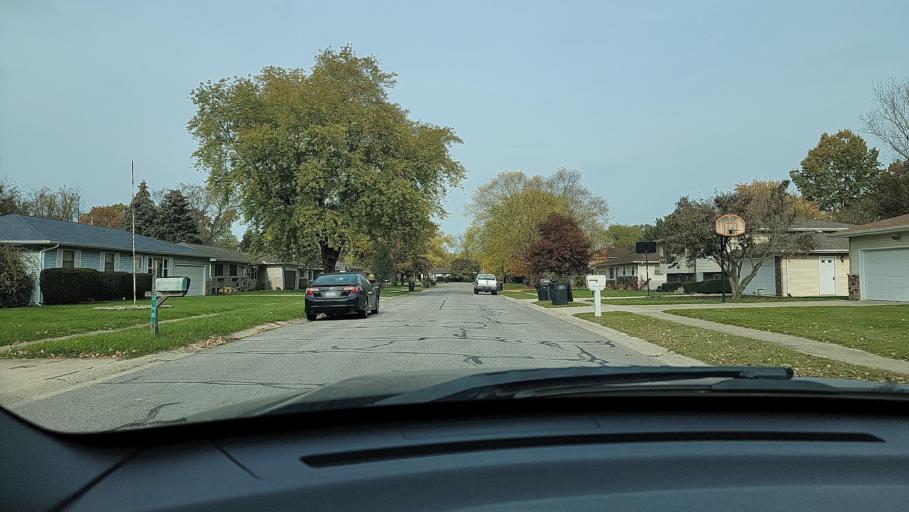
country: US
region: Indiana
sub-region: Porter County
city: Portage
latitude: 41.5882
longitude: -87.1705
